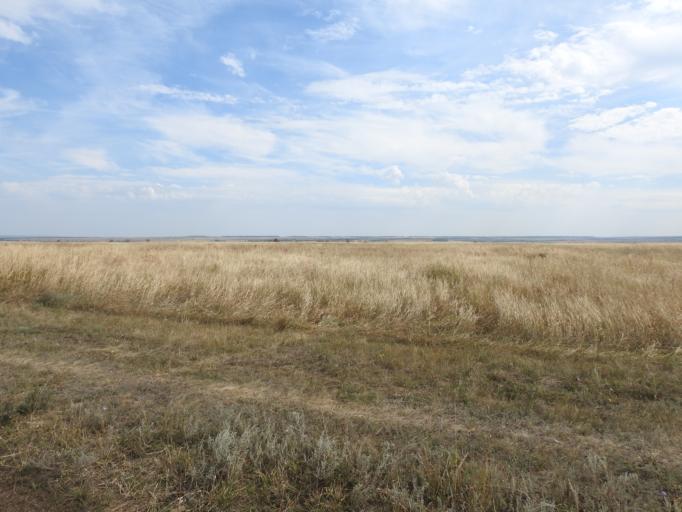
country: RU
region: Volgograd
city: Zhirnovsk
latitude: 51.2084
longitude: 44.9295
